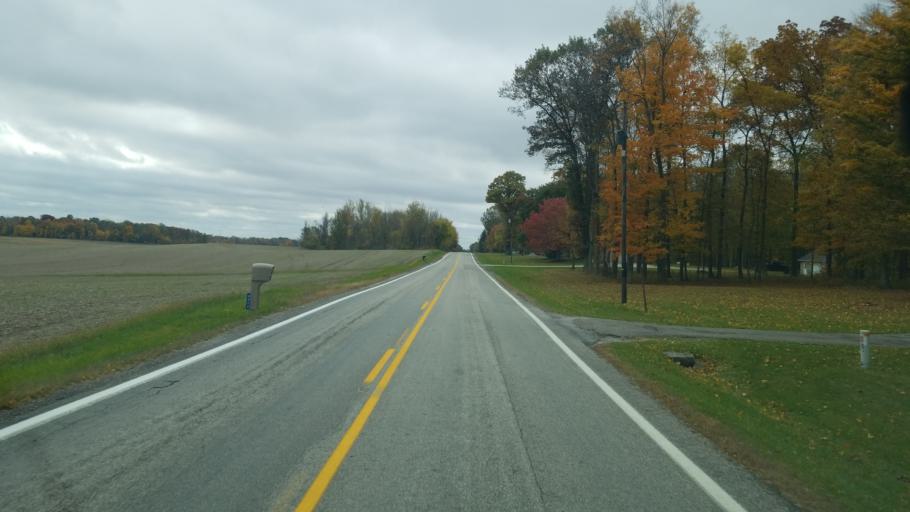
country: US
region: Ohio
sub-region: Crawford County
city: Crestline
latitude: 40.8820
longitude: -82.7612
